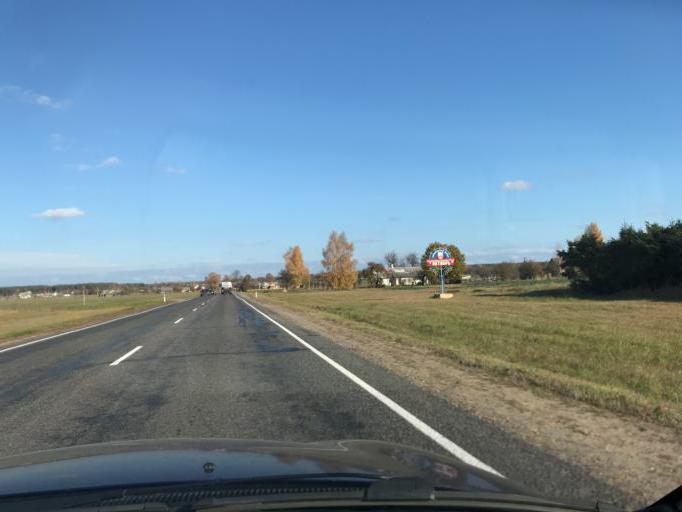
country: BY
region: Grodnenskaya
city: Lida
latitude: 54.0076
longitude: 25.2161
